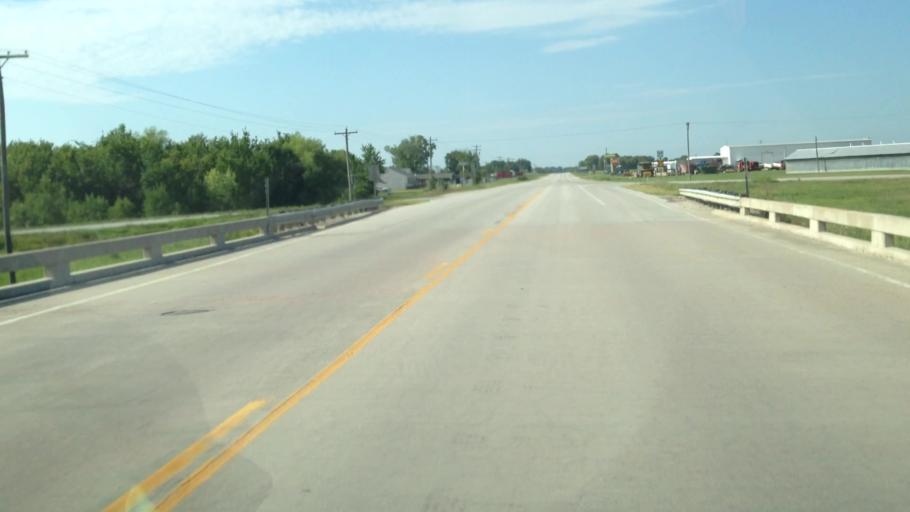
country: US
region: Kansas
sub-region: Neosho County
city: Erie
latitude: 37.5145
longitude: -95.2699
